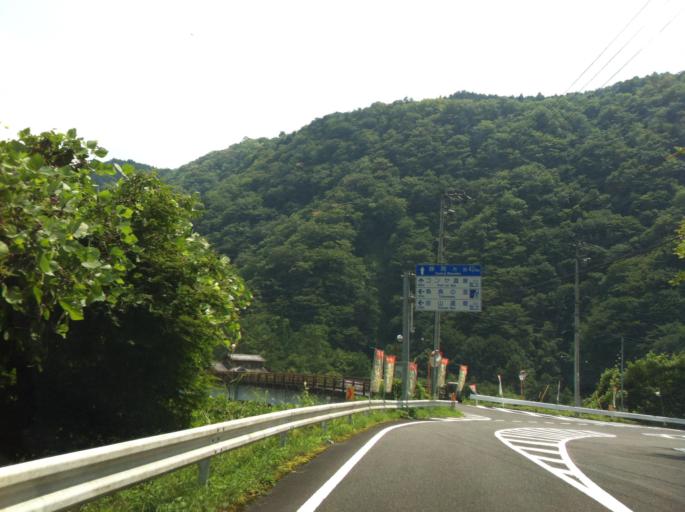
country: JP
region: Shizuoka
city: Fujinomiya
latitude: 35.2805
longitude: 138.3383
